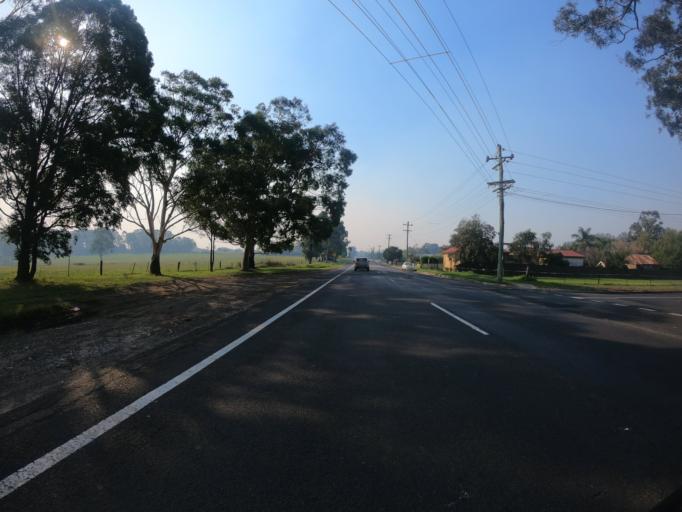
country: AU
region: New South Wales
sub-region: Wollondilly
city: Douglas Park
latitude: -34.2053
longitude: 150.7854
